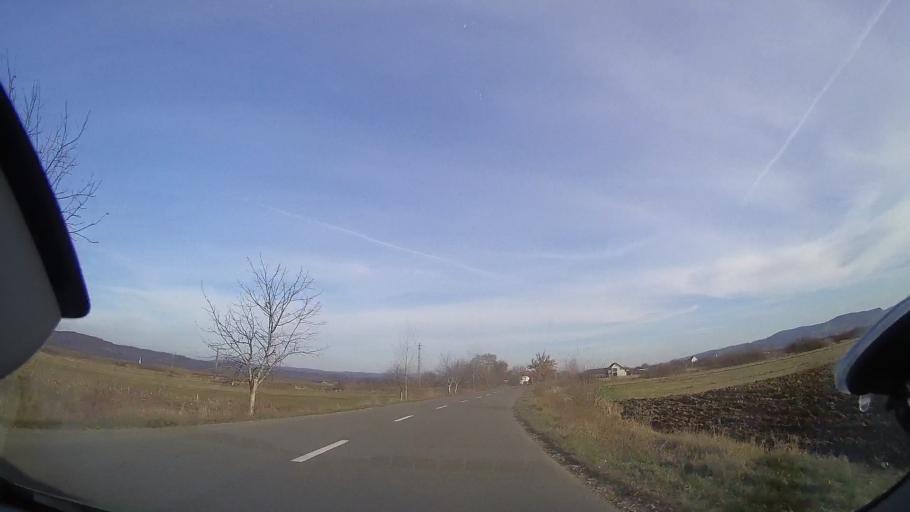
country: RO
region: Bihor
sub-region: Comuna Tetchea
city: Hotar
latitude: 47.0557
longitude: 22.2627
